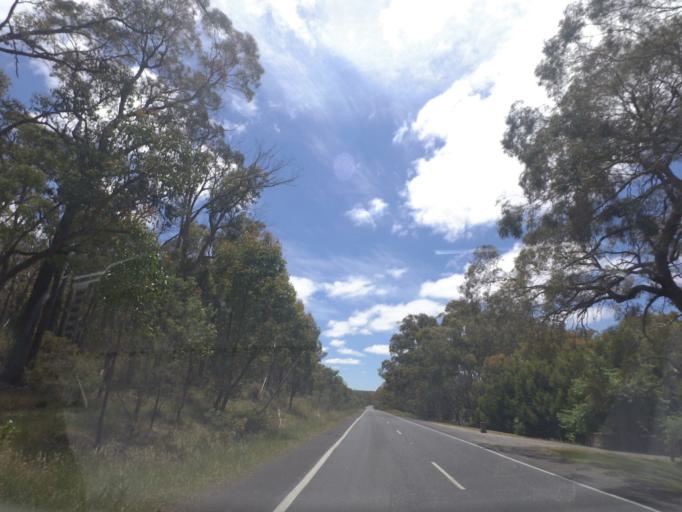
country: AU
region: Victoria
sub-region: Mount Alexander
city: Castlemaine
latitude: -37.3057
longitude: 144.1641
